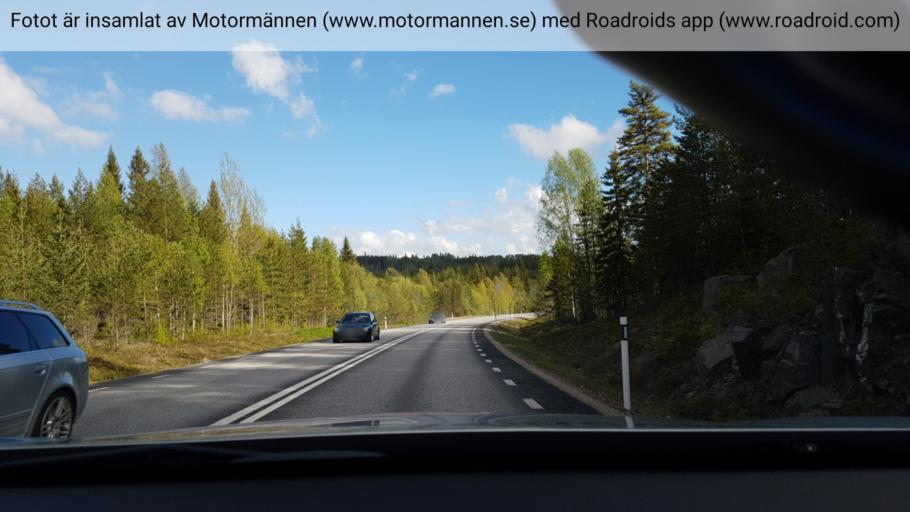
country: SE
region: Dalarna
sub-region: Faluns Kommun
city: Bjursas
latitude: 60.7831
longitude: 15.3098
